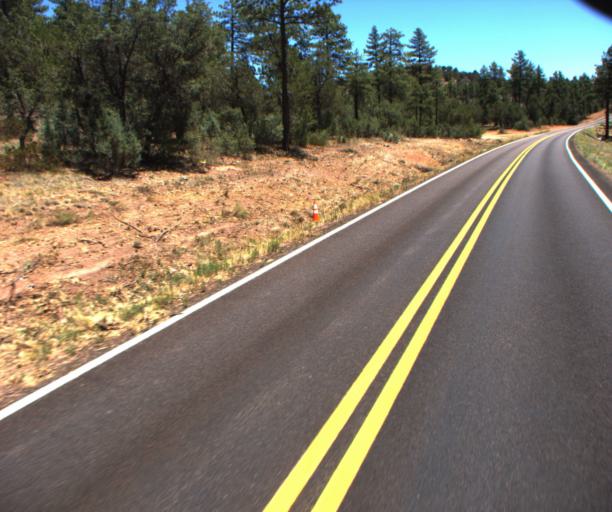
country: US
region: Arizona
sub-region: Gila County
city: Pine
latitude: 34.3674
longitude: -111.4355
